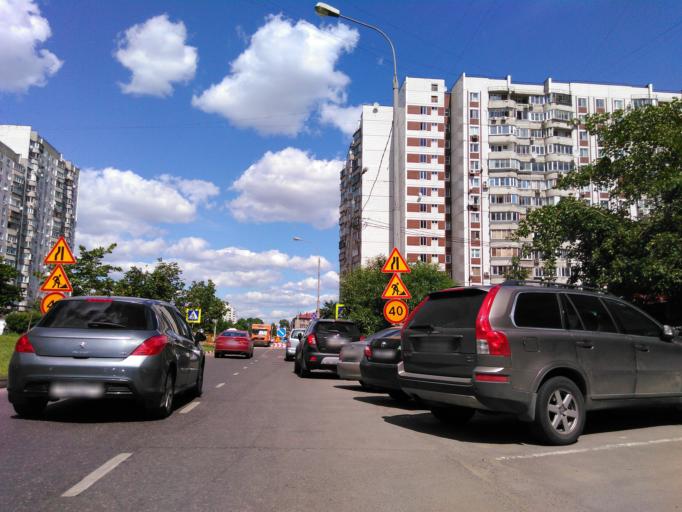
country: RU
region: Moscow
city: Novyye Cheremushki
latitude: 55.6819
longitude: 37.5798
